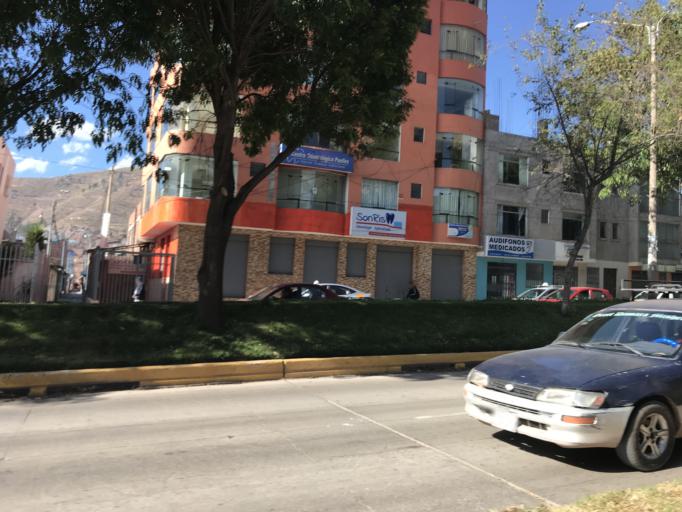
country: PE
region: Cusco
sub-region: Provincia de Cusco
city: Cusco
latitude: -13.5325
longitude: -71.9609
